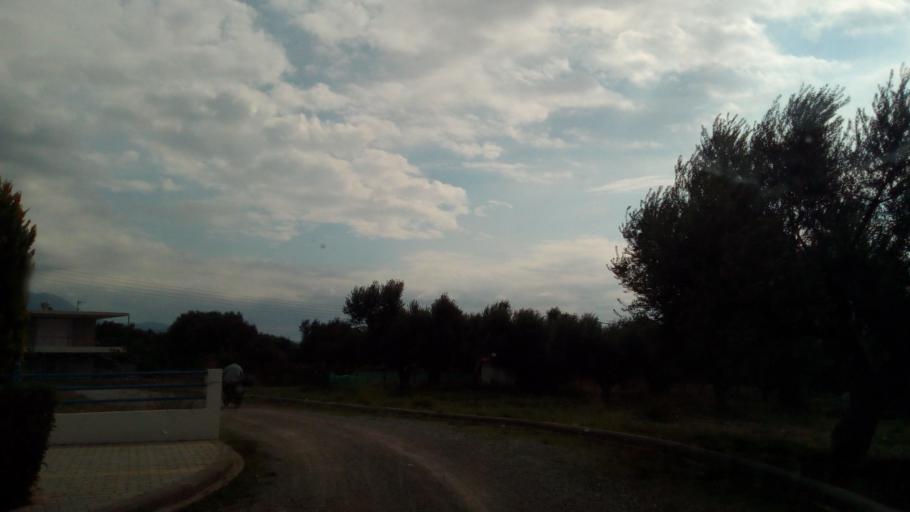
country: GR
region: West Greece
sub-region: Nomos Achaias
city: Kamarai
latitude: 38.3957
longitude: 22.0058
